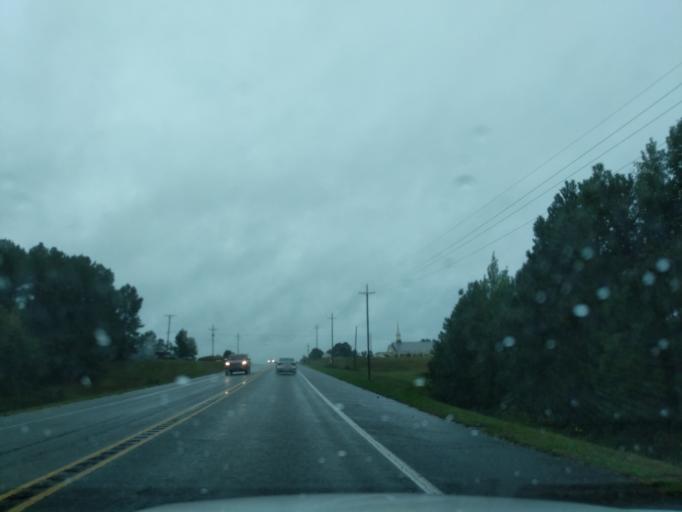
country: US
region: Louisiana
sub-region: Webster Parish
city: Minden
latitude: 32.6123
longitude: -93.2498
